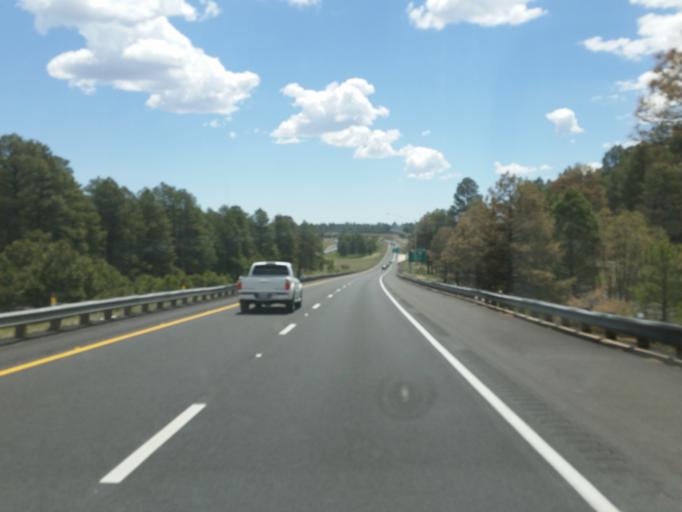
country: US
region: Arizona
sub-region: Coconino County
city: Flagstaff
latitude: 35.1761
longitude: -111.6741
